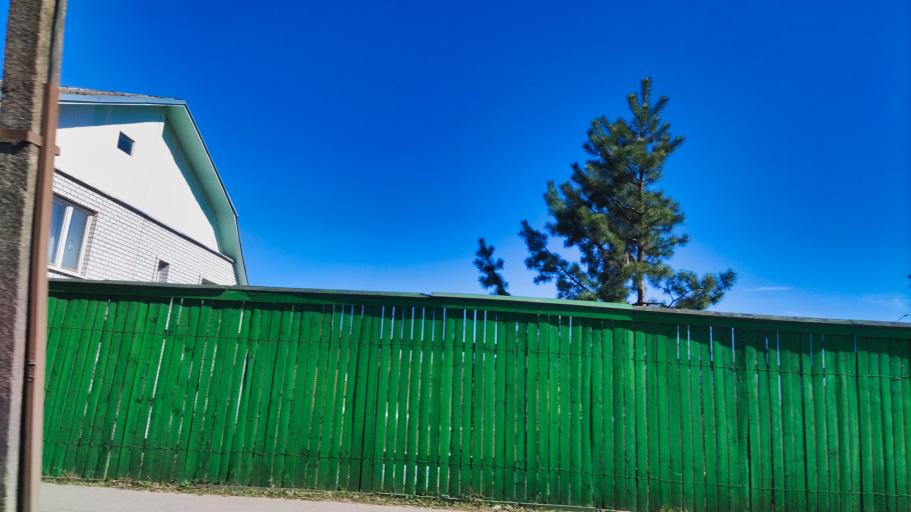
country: RU
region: Tverskaya
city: Rzhev
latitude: 56.2555
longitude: 34.3359
